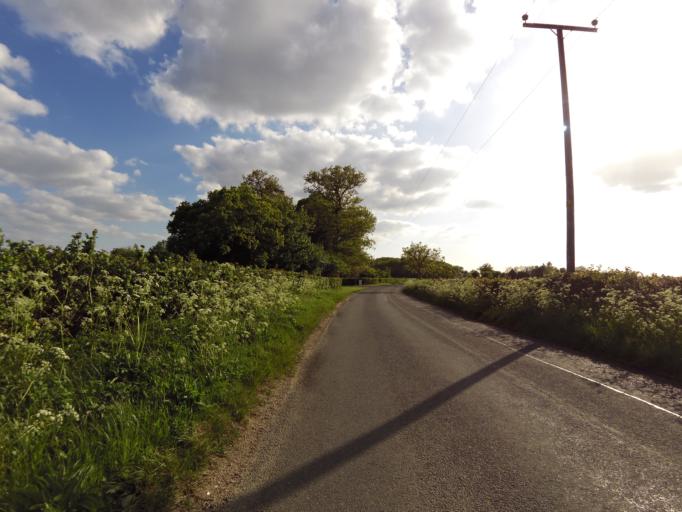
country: GB
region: England
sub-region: Suffolk
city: Beccles
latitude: 52.4270
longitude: 1.5307
